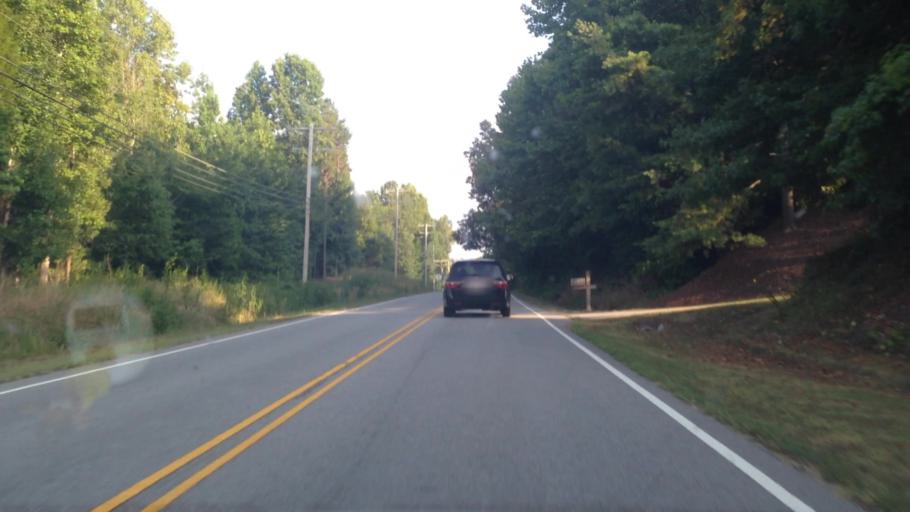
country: US
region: North Carolina
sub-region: Davidson County
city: Thomasville
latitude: 35.9462
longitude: -80.0757
